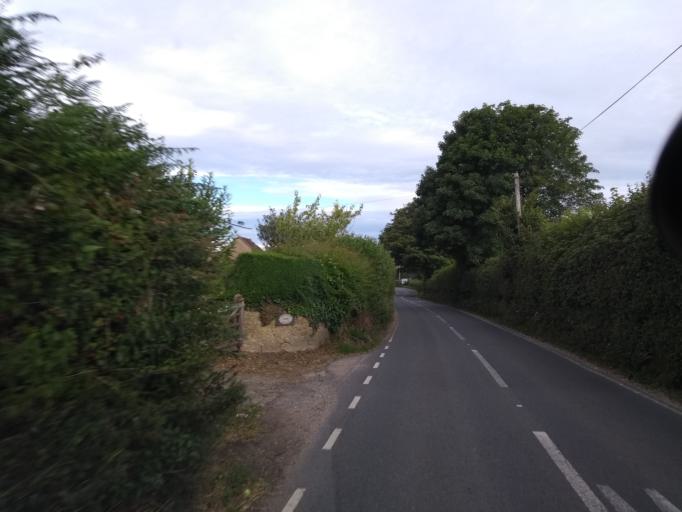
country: GB
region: England
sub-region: Dorset
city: Beaminster
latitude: 50.8336
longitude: -2.7720
